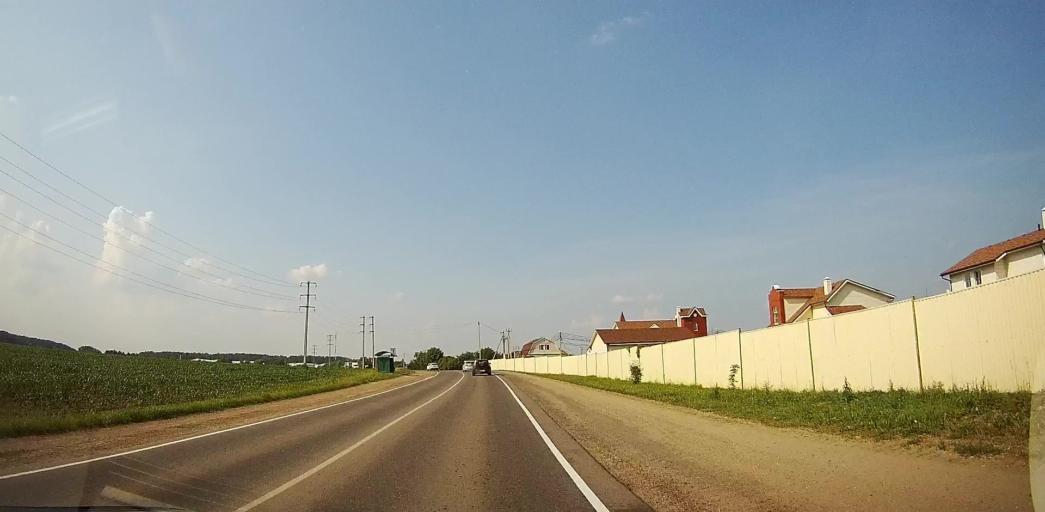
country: RU
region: Moskovskaya
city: Barybino
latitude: 55.2961
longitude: 37.9124
